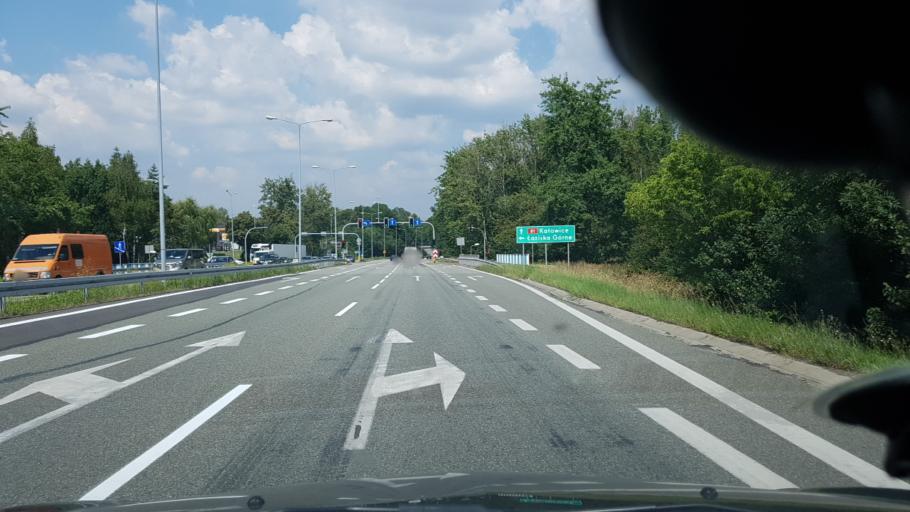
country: PL
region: Silesian Voivodeship
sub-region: Powiat mikolowski
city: Laziska Gorne
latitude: 50.1565
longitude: 18.8490
